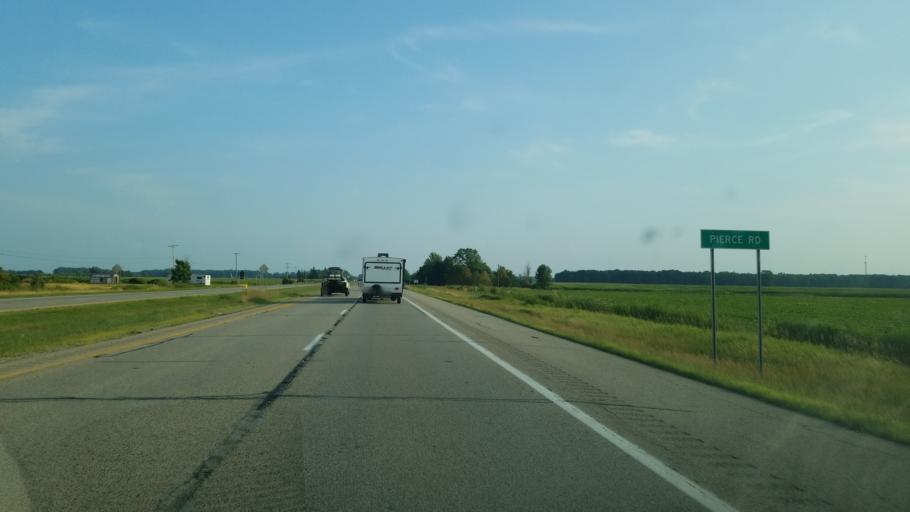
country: US
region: Michigan
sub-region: Gratiot County
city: Ithaca
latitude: 43.2649
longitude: -84.5633
